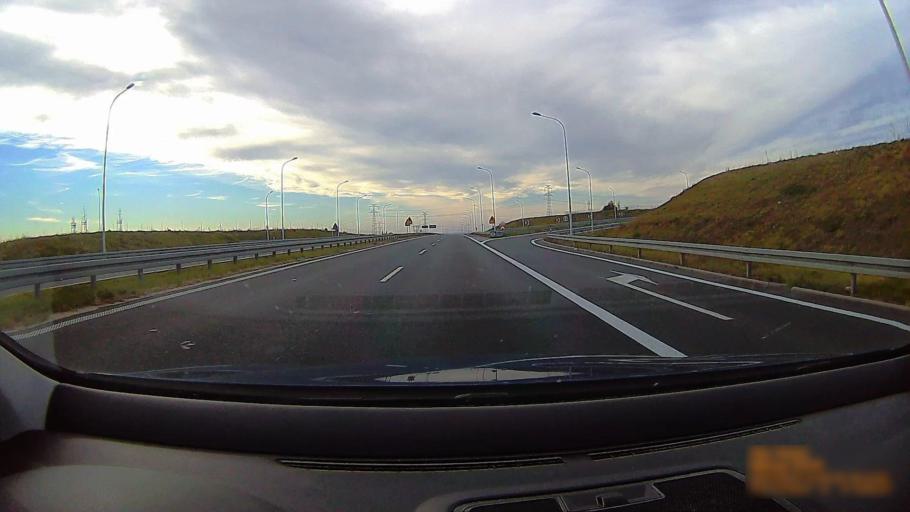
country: PL
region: Greater Poland Voivodeship
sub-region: Powiat ostrowski
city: Przygodzice
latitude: 51.6299
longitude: 17.8685
